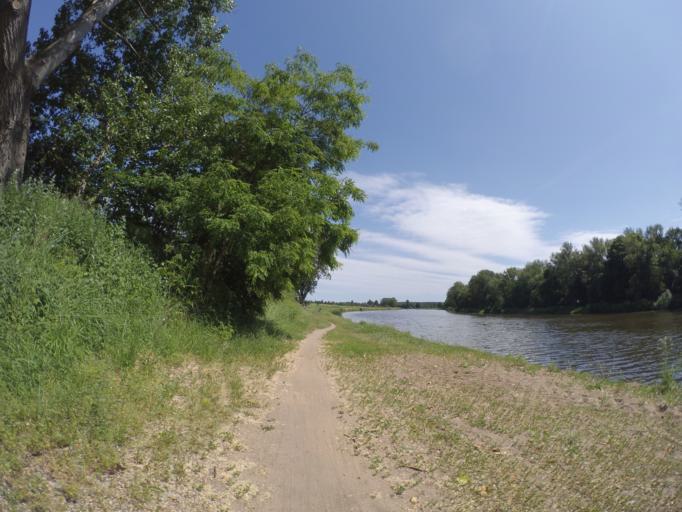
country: CZ
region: Central Bohemia
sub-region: Okres Nymburk
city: Sadska
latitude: 50.1686
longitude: 14.9512
